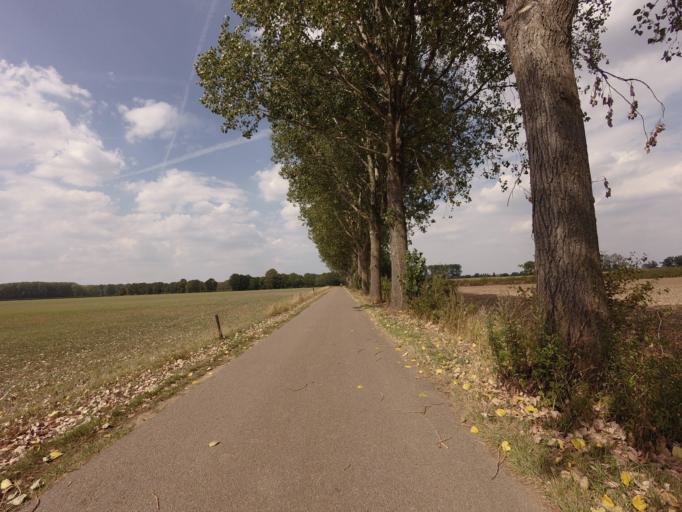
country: NL
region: Gelderland
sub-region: Gemeente Rheden
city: Ellecom
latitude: 52.0088
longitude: 6.1021
